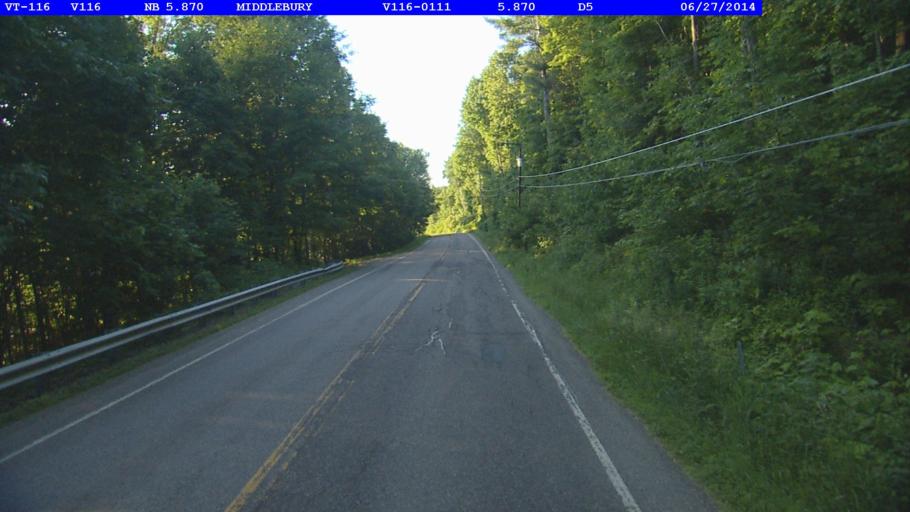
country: US
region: Vermont
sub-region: Addison County
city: Middlebury (village)
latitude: 44.0446
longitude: -73.0904
